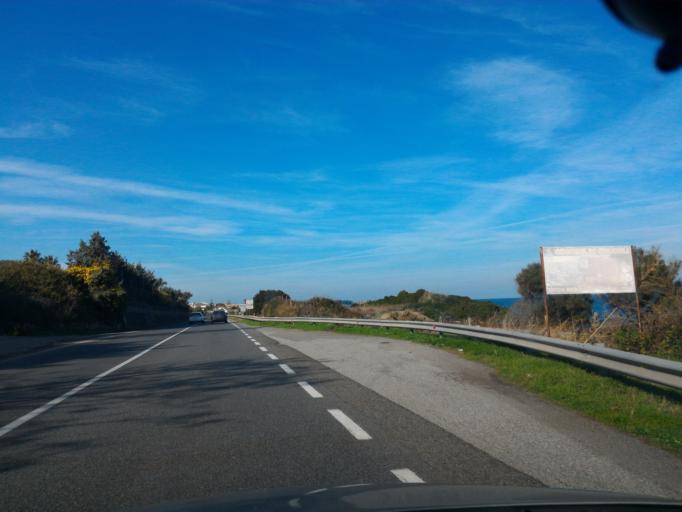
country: IT
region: Calabria
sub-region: Provincia di Crotone
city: Torretta
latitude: 39.4410
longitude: 17.0485
